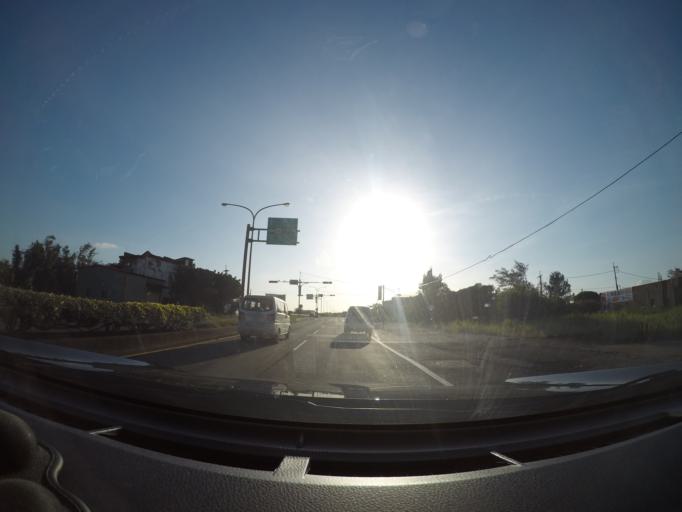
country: TW
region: Taiwan
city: Taoyuan City
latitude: 25.0764
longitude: 121.2046
